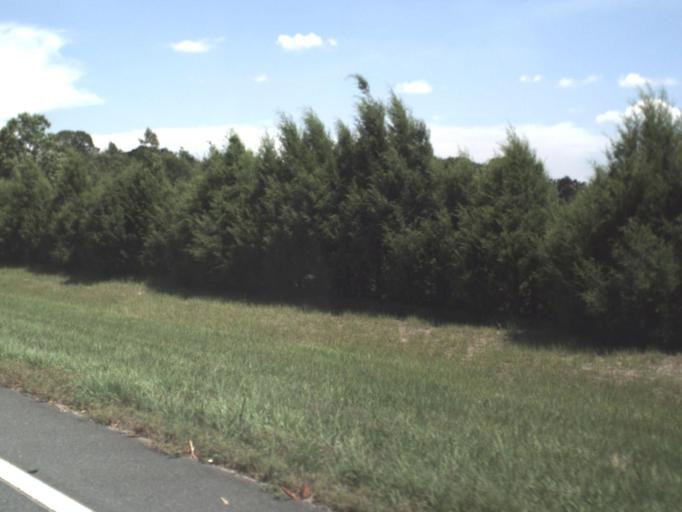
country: US
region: Florida
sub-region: Lafayette County
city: Mayo
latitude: 30.1275
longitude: -83.2774
